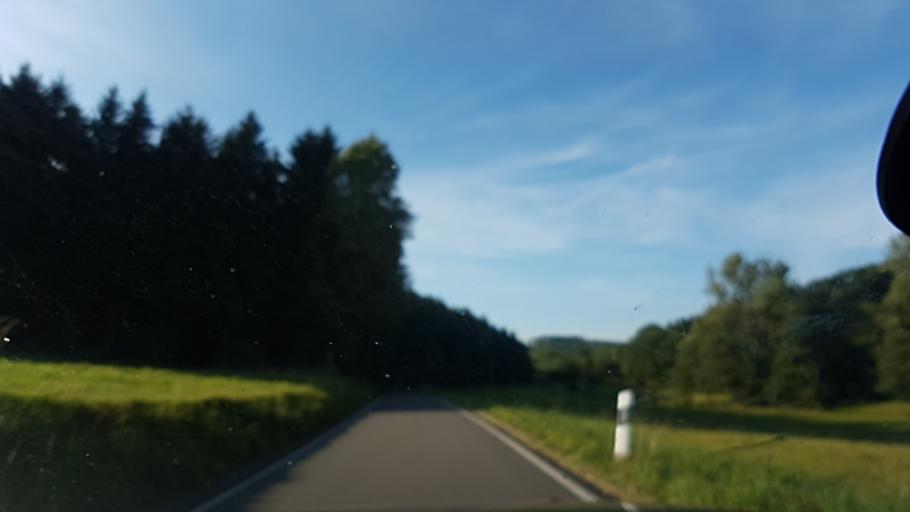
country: DE
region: North Rhine-Westphalia
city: Kierspe
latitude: 51.1380
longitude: 7.5726
